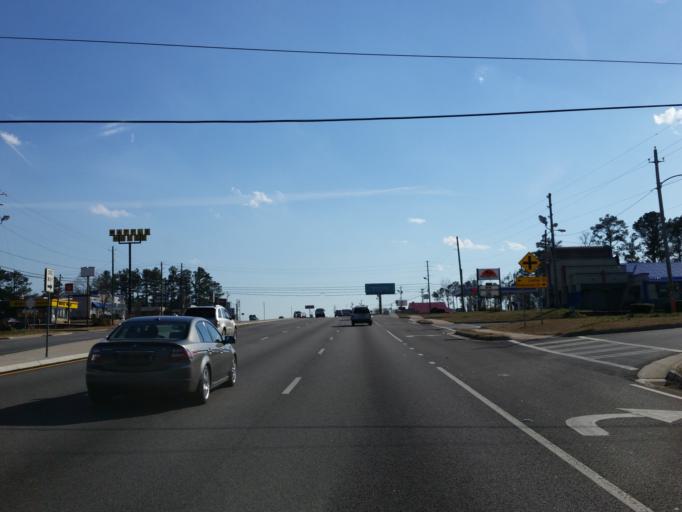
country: US
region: Georgia
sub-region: Spalding County
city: Experiment
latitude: 33.2820
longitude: -84.2920
